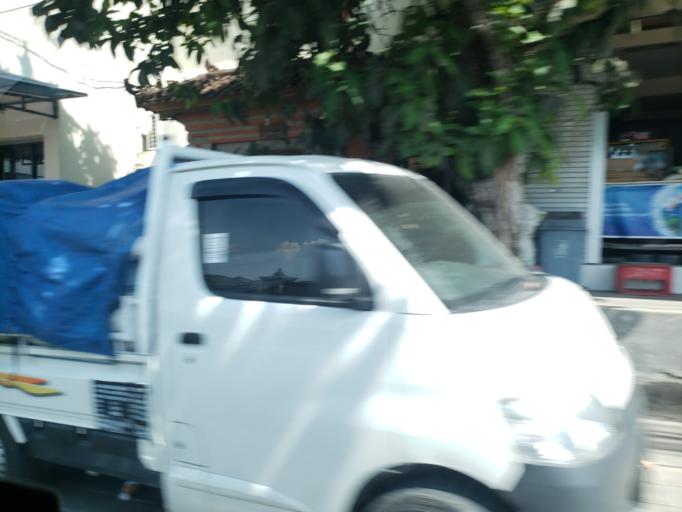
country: ID
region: Bali
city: Kangin
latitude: -8.8237
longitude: 115.1423
